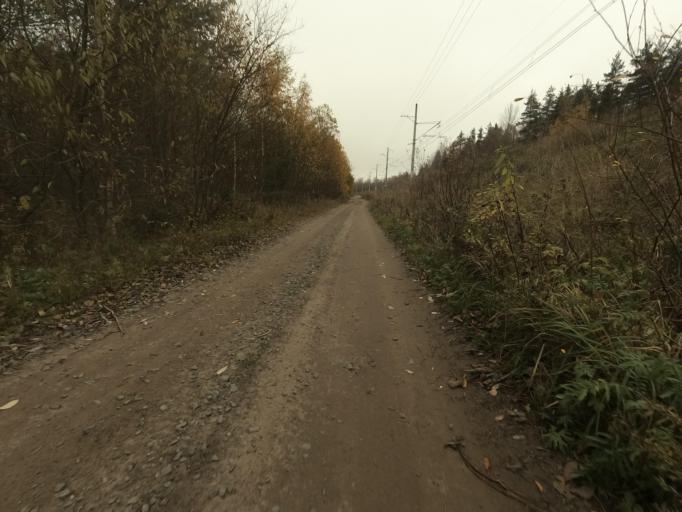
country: RU
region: Leningrad
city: Pavlovo
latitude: 59.7808
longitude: 30.8969
